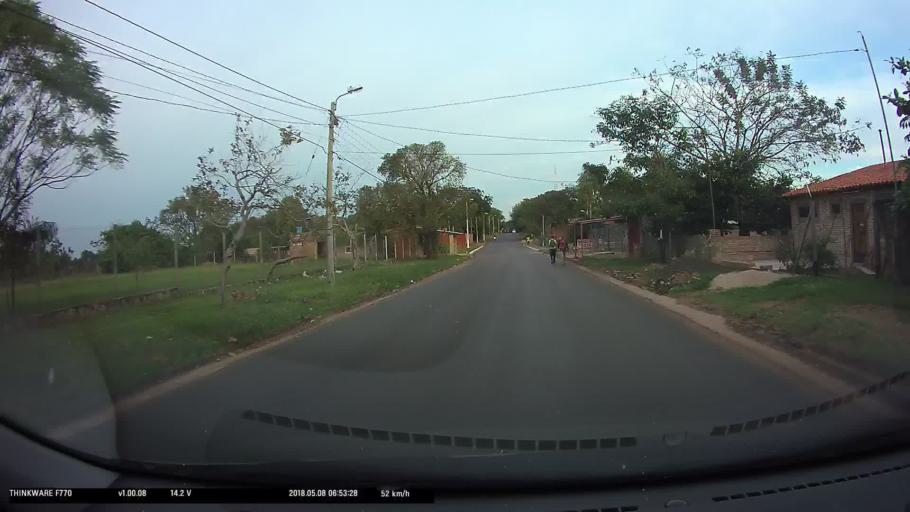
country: PY
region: Central
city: Limpio
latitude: -25.2352
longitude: -57.4708
